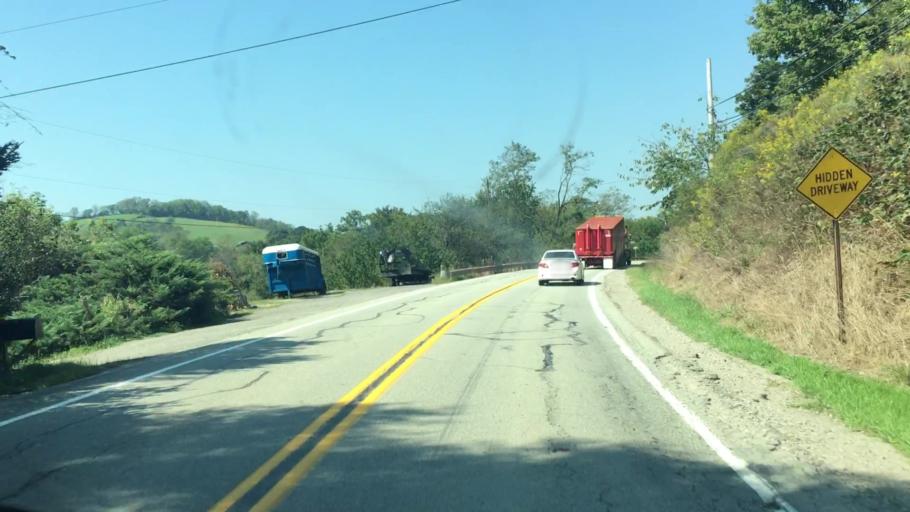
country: US
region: Pennsylvania
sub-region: Washington County
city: Washington
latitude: 40.0435
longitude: -80.2878
